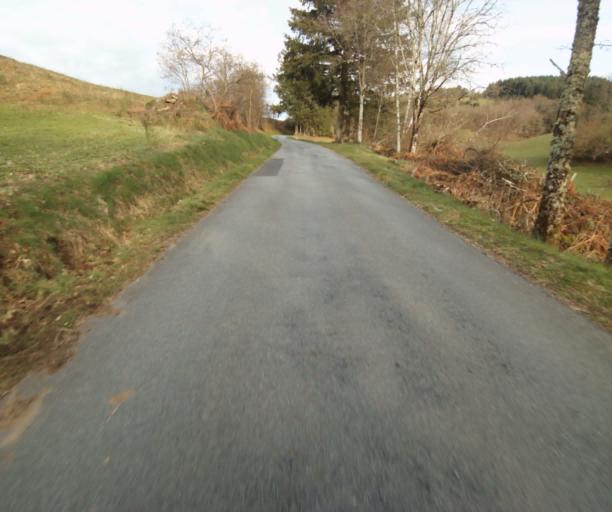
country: FR
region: Limousin
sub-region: Departement de la Correze
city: Correze
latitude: 45.4138
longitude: 1.9114
